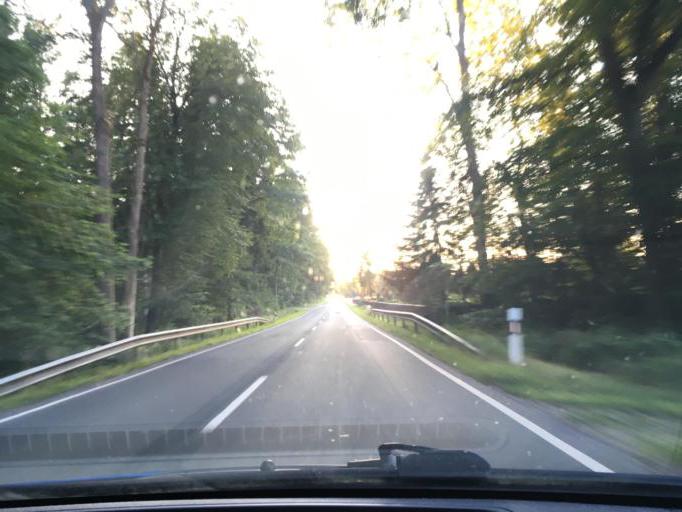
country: DE
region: Lower Saxony
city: Rehlingen
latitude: 53.1179
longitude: 10.2253
